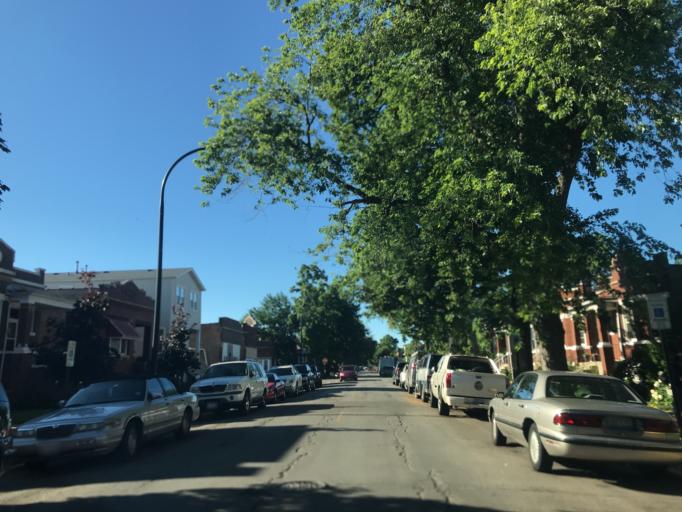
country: US
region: Illinois
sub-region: Cook County
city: Cicero
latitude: 41.8466
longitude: -87.7687
